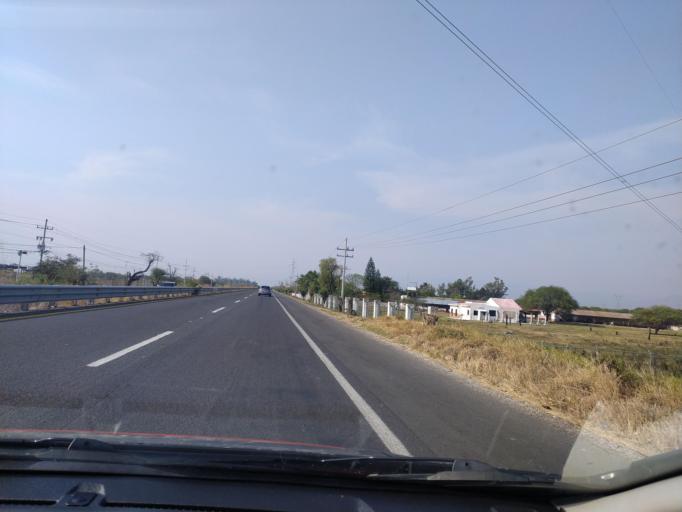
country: MX
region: Jalisco
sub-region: Acatlan de Juarez
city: Villa de los Ninos
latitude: 20.3855
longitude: -103.5931
